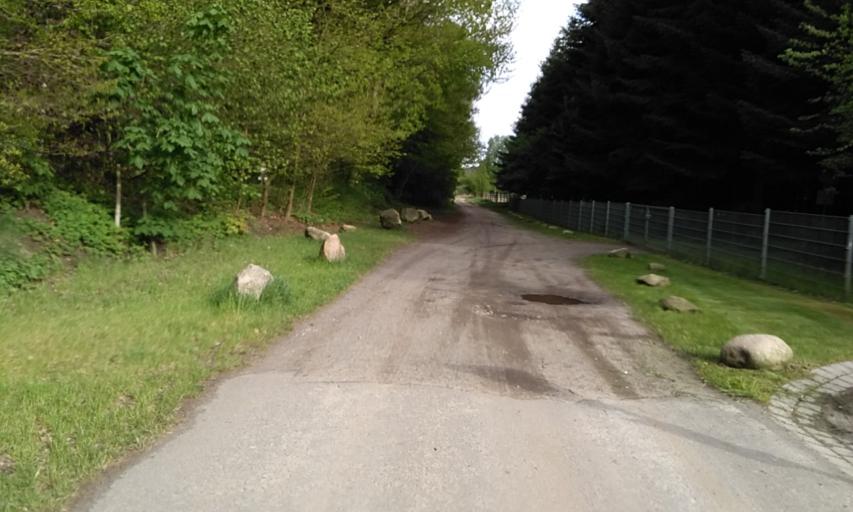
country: DE
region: Lower Saxony
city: Buxtehude
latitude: 53.4489
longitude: 9.6718
